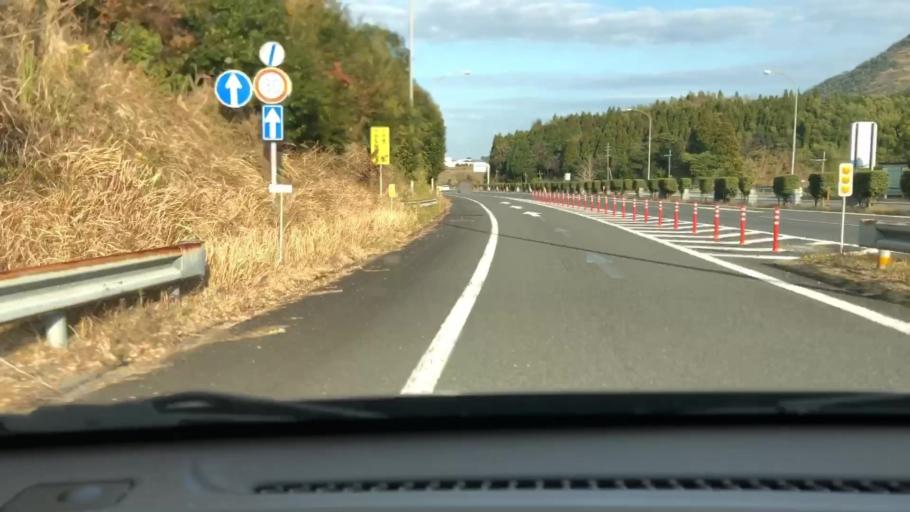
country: JP
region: Miyazaki
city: Miyazaki-shi
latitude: 31.8221
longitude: 131.3039
